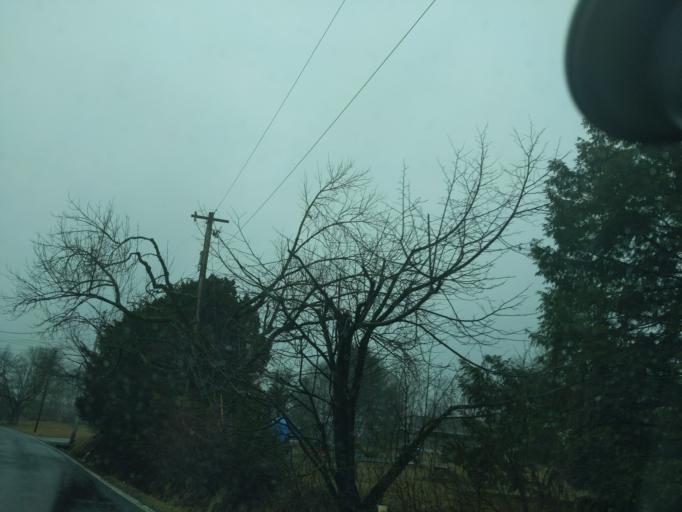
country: US
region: Pennsylvania
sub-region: Bucks County
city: Quakertown
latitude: 40.4402
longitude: -75.3708
